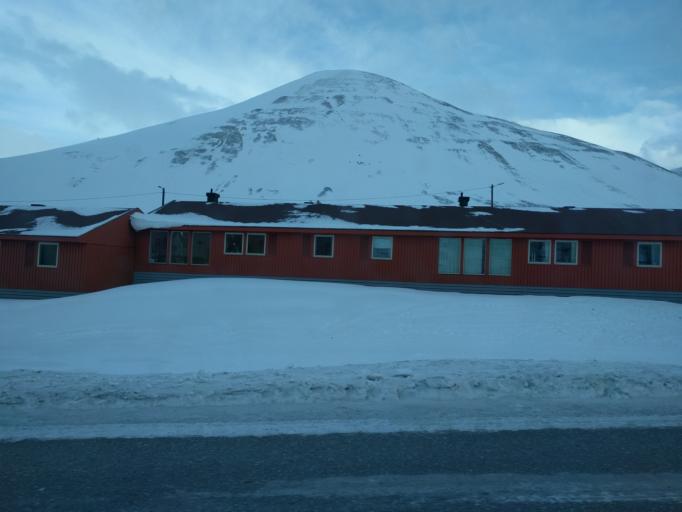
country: SJ
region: Svalbard
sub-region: Spitsbergen
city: Longyearbyen
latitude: 78.2161
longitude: 15.6275
